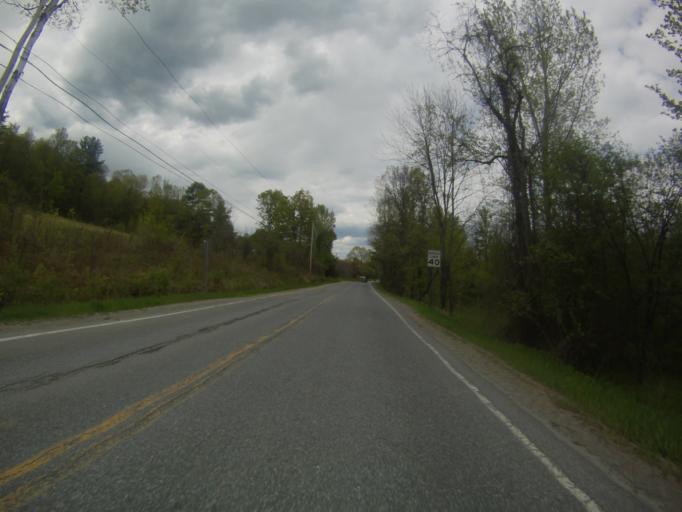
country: US
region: New York
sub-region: Essex County
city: Port Henry
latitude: 44.0336
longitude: -73.5027
